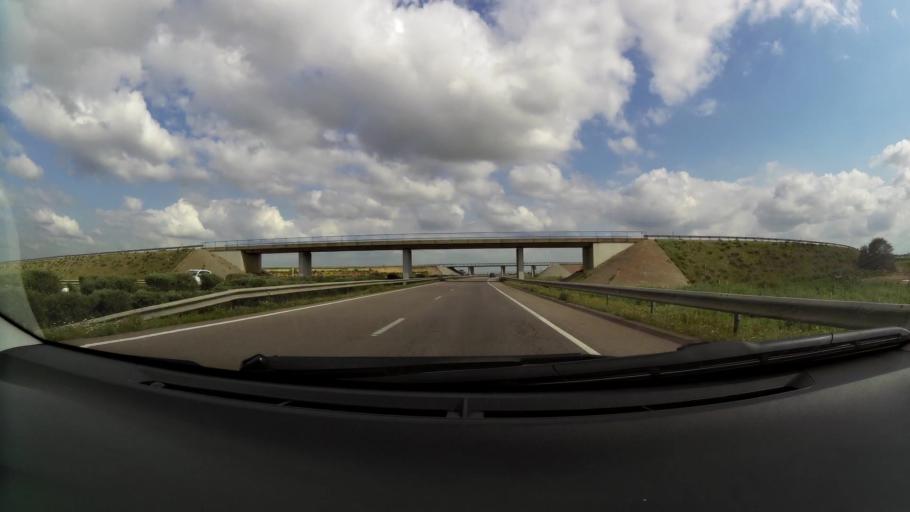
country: MA
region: Chaouia-Ouardigha
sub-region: Settat Province
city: Berrechid
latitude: 33.2904
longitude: -7.5497
